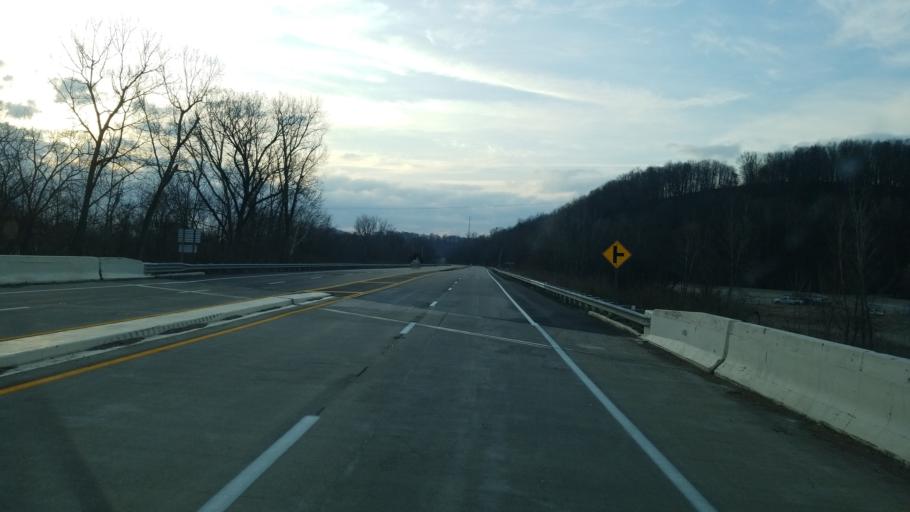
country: US
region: Ohio
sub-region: Ross County
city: Chillicothe
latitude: 39.3069
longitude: -82.9599
